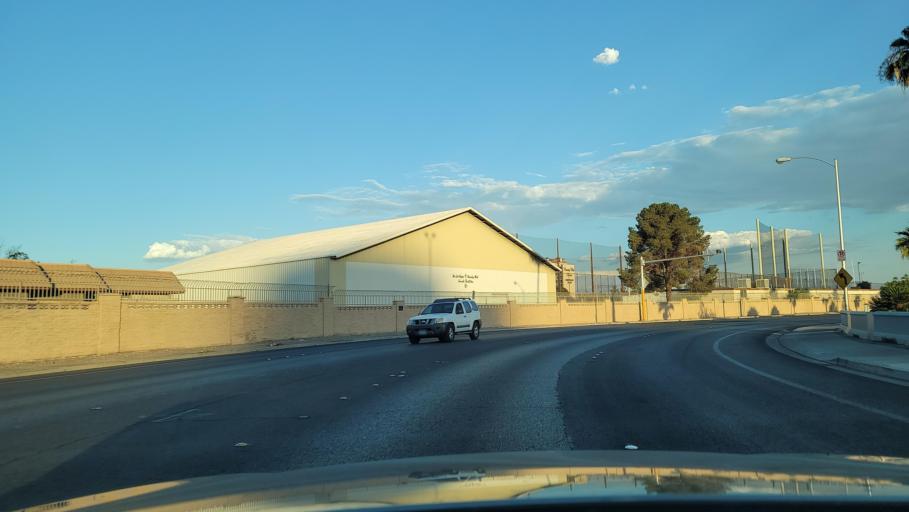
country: US
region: Nevada
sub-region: Clark County
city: Winchester
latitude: 36.1333
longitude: -115.1480
